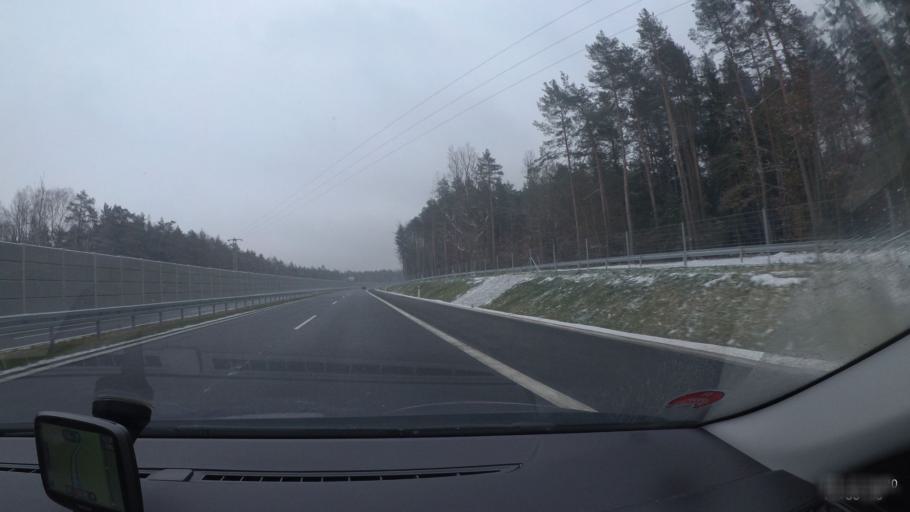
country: CZ
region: Central Bohemia
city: Revnicov
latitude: 50.1748
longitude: 13.8259
